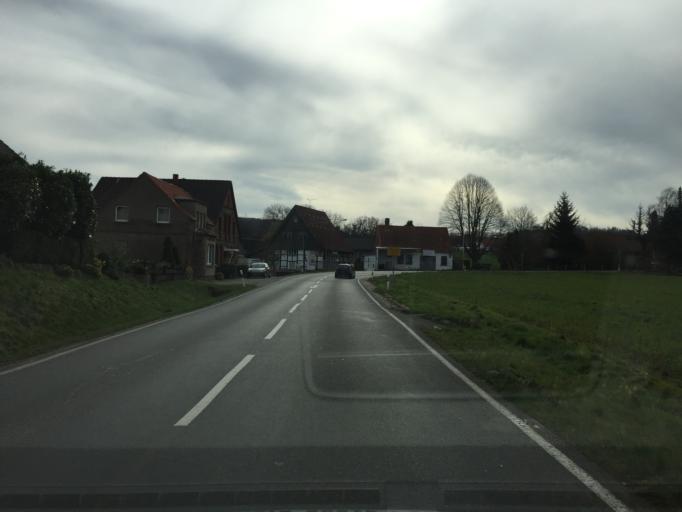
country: DE
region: North Rhine-Westphalia
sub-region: Regierungsbezirk Detmold
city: Bad Salzuflen
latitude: 52.1043
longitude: 8.7955
